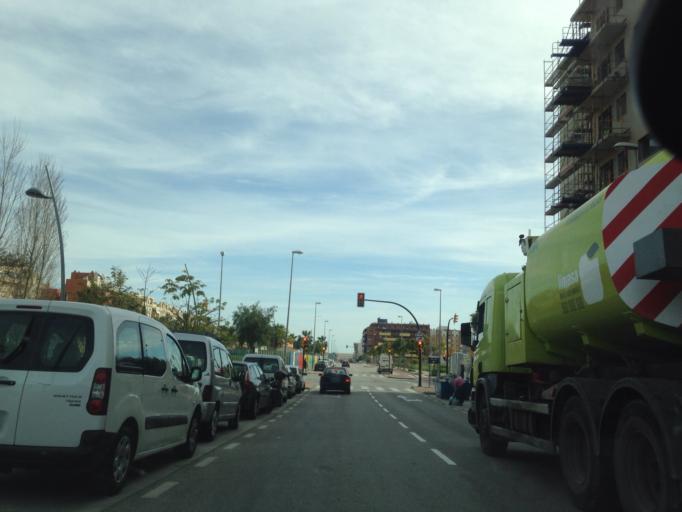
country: ES
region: Andalusia
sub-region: Provincia de Malaga
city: Malaga
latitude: 36.7262
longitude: -4.4634
